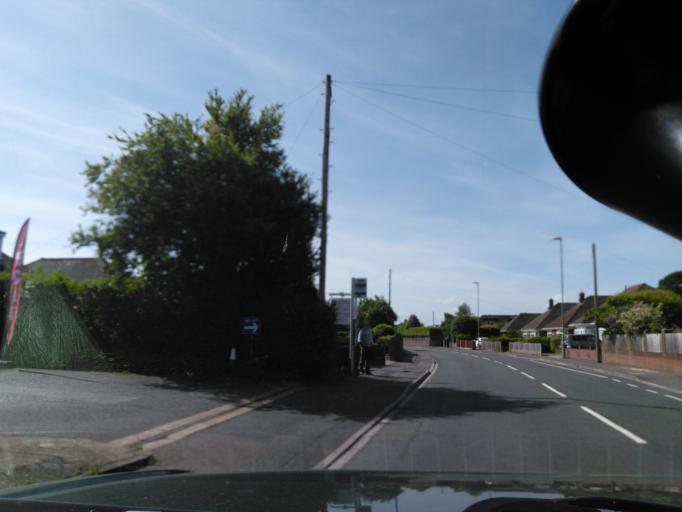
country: GB
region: England
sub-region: Hampshire
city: Lee-on-the-Solent
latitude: 50.8219
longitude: -1.2148
